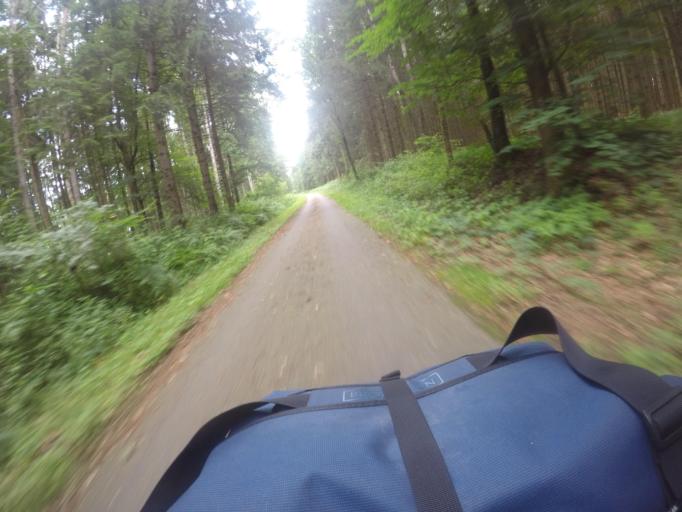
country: DE
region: Bavaria
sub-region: Swabia
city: Kellmunz
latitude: 48.1176
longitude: 10.1525
